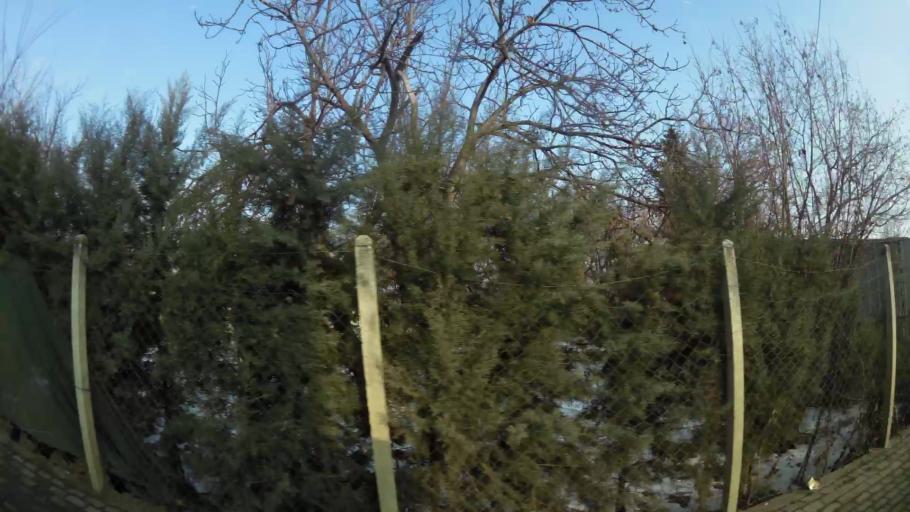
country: MK
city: Creshevo
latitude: 42.0272
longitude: 21.5137
